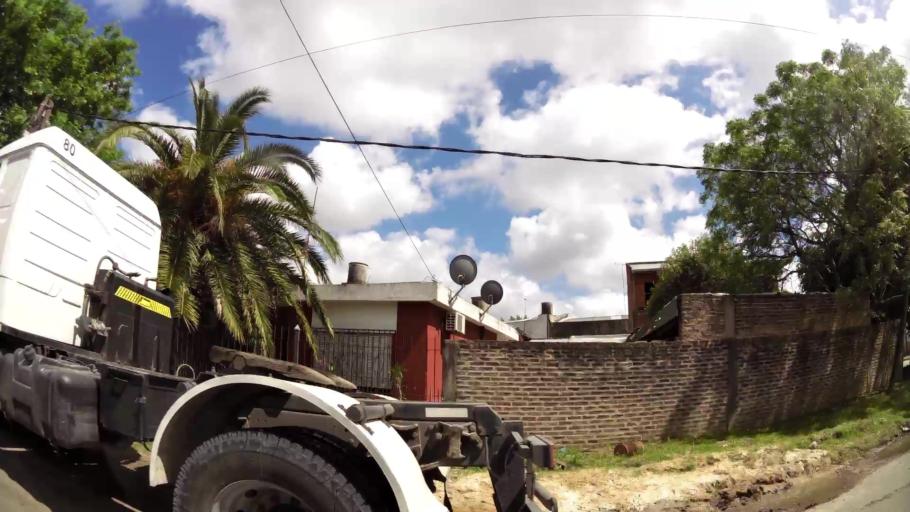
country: AR
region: Buenos Aires
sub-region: Partido de Quilmes
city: Quilmes
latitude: -34.8365
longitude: -58.1811
